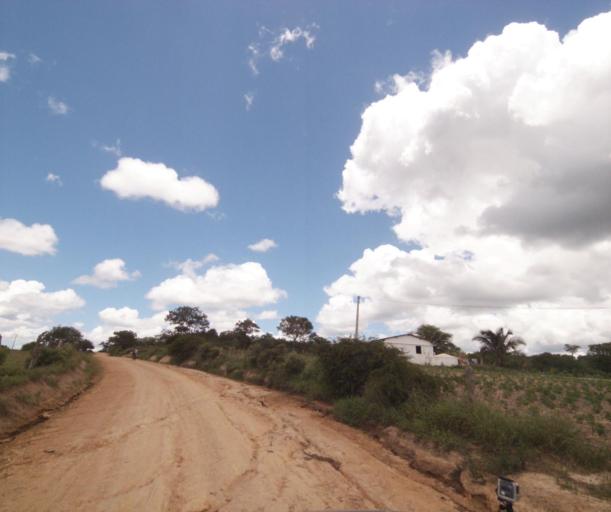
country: BR
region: Bahia
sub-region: Pocoes
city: Pocoes
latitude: -14.3789
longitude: -40.3625
